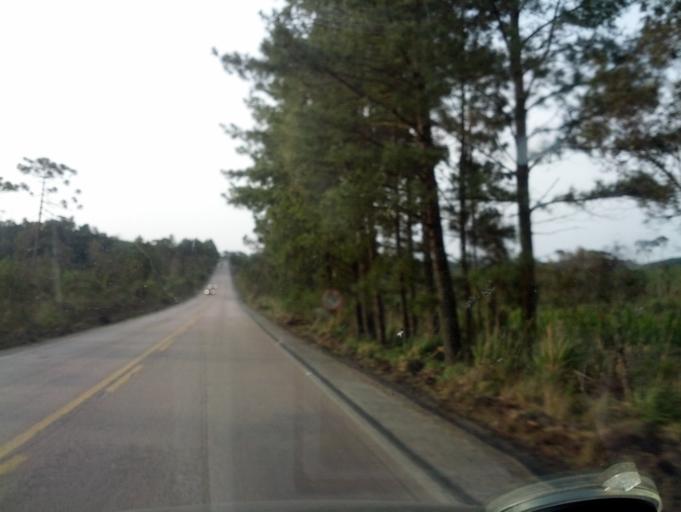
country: BR
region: Santa Catarina
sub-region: Otacilio Costa
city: Otacilio Costa
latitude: -27.3468
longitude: -50.1305
